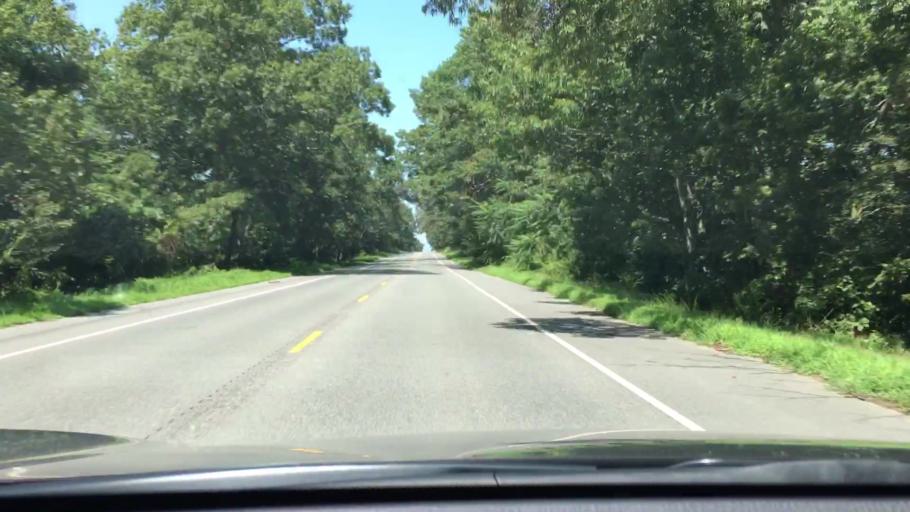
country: US
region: New Jersey
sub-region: Cumberland County
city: Laurel Lake
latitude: 39.3504
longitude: -75.0533
